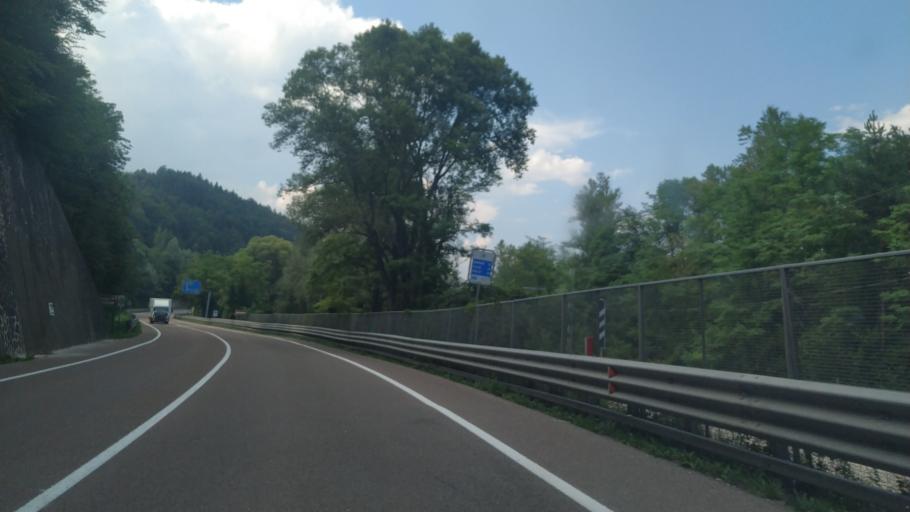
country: IT
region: Trentino-Alto Adige
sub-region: Provincia di Trento
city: Denno
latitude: 46.2573
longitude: 11.0585
